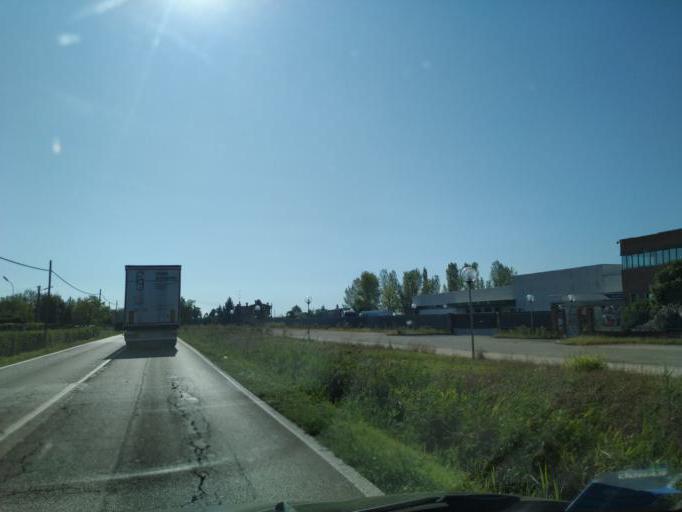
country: IT
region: Emilia-Romagna
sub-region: Provincia di Bologna
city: Sant'Agata Bolognese
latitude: 44.6546
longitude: 11.1421
